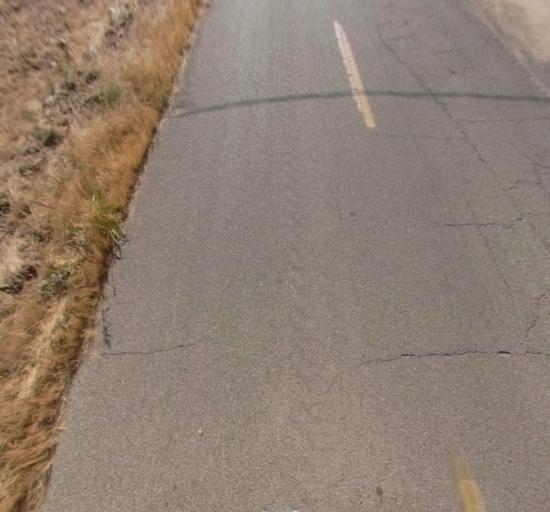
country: US
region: California
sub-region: Madera County
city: Fairmead
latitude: 37.0110
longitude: -120.1686
